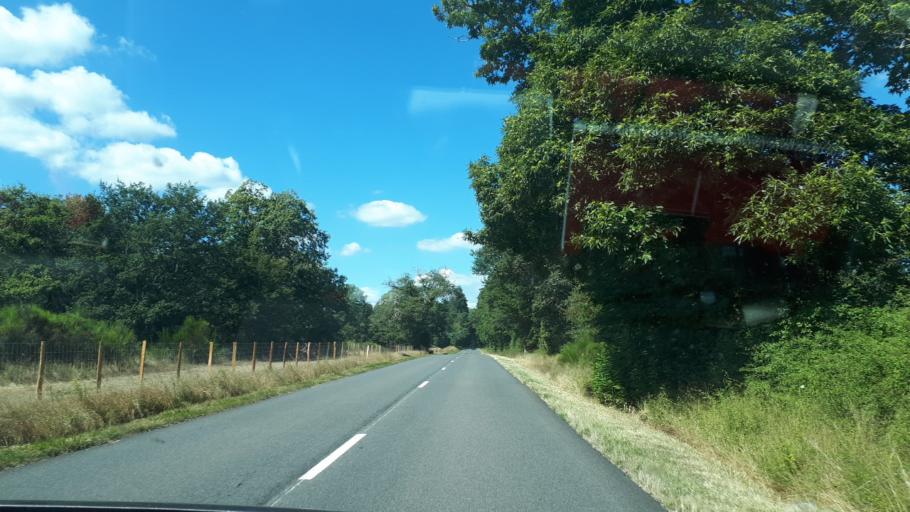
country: FR
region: Centre
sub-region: Departement du Loir-et-Cher
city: Chaumont-sur-Tharonne
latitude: 47.5763
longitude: 1.9395
